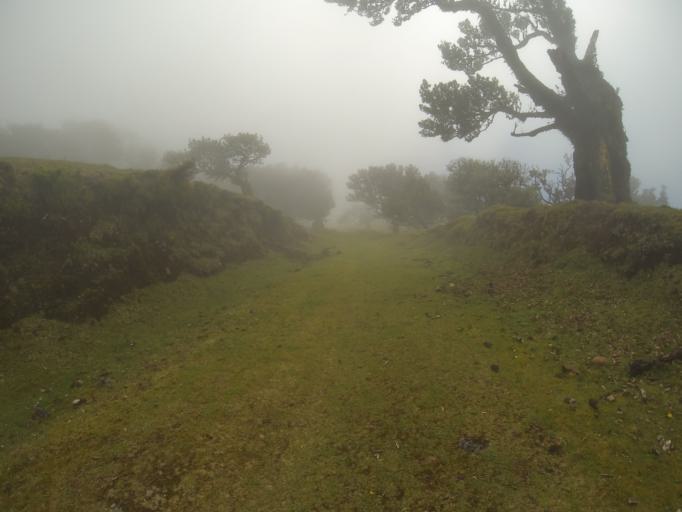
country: PT
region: Madeira
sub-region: Porto Moniz
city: Porto Moniz
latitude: 32.8118
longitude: -17.1423
